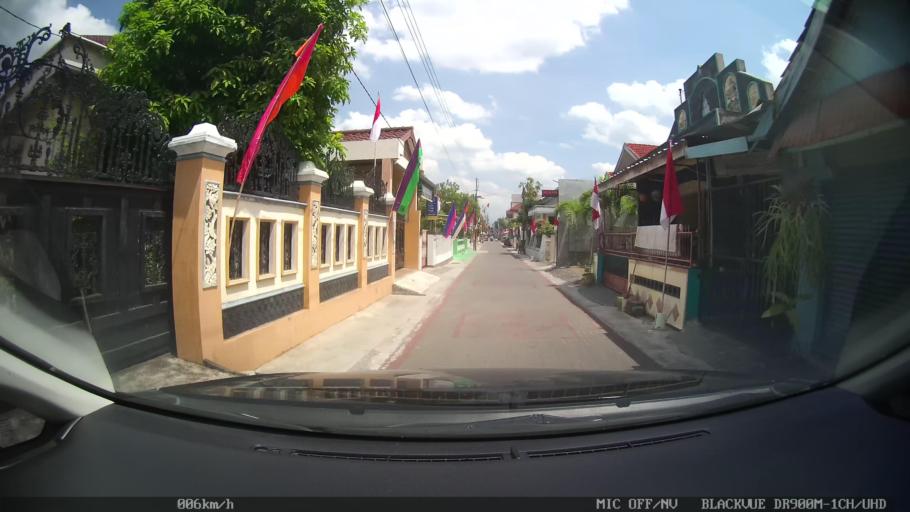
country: ID
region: Daerah Istimewa Yogyakarta
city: Yogyakarta
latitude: -7.8069
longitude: 110.3530
